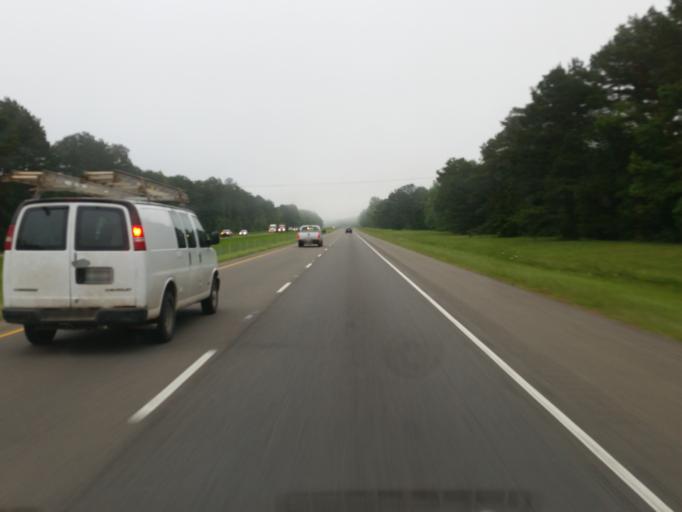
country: US
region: Louisiana
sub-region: Bossier Parish
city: Haughton
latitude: 32.5768
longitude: -93.4647
